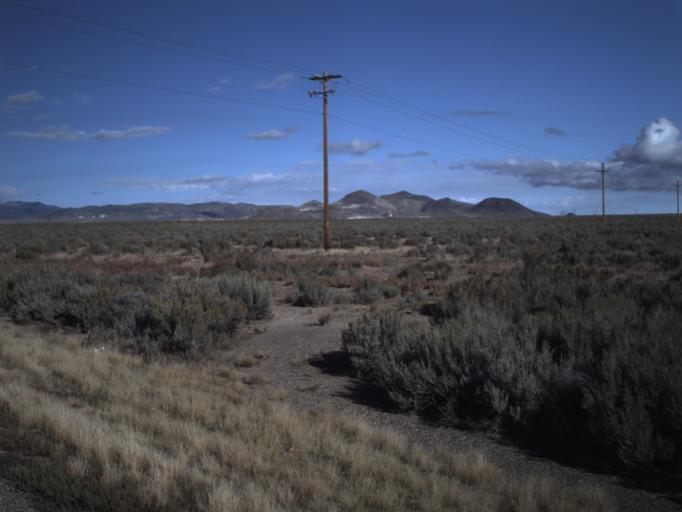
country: US
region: Utah
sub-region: Beaver County
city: Milford
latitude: 38.4015
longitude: -113.0372
